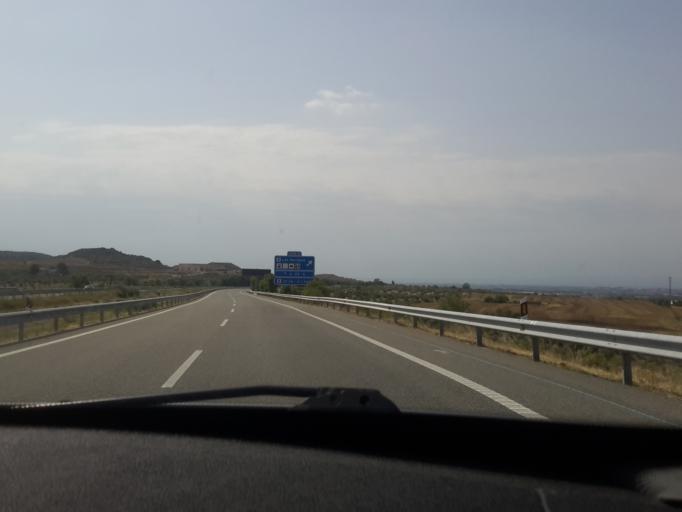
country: ES
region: Catalonia
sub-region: Provincia de Lleida
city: Arbeca
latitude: 41.4787
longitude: 0.8790
